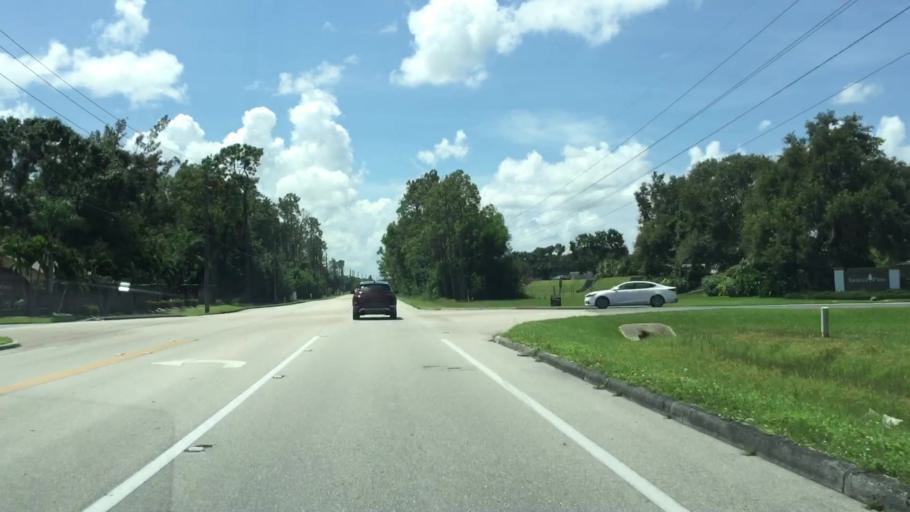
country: US
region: Florida
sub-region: Lee County
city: Villas
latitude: 26.5584
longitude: -81.8468
